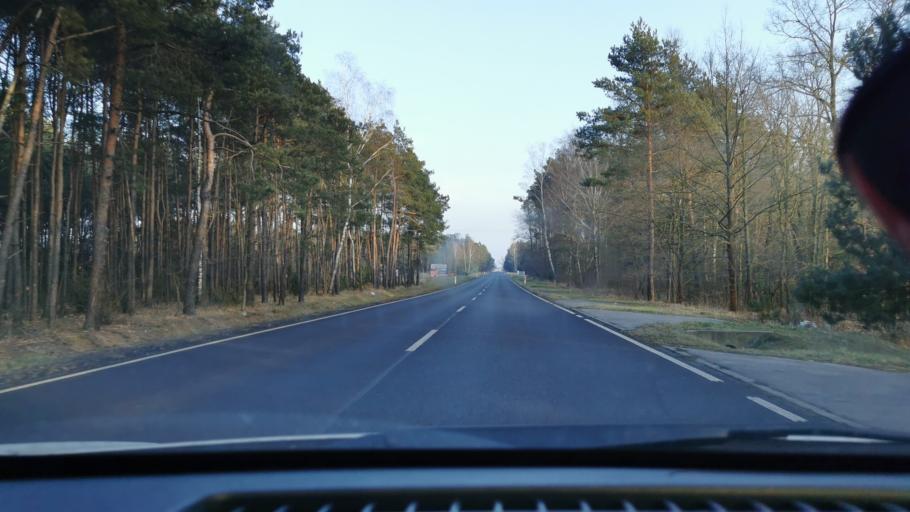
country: PL
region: Lodz Voivodeship
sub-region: Powiat pabianicki
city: Dlutow
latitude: 51.5118
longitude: 19.3478
